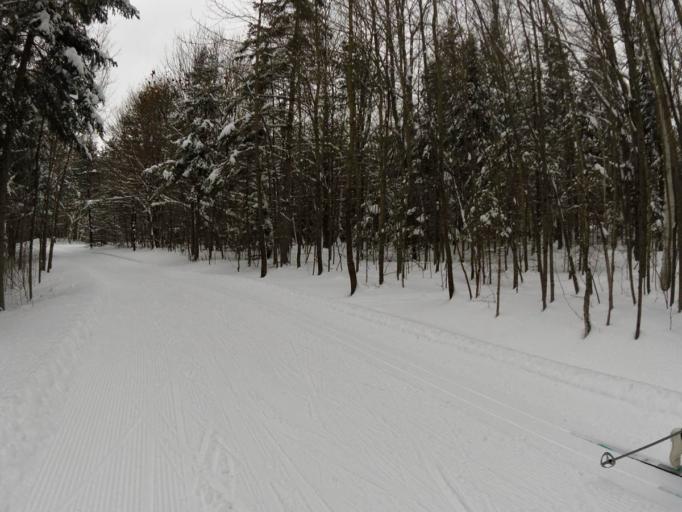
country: CA
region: Quebec
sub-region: Outaouais
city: Wakefield
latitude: 45.6016
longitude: -76.0201
